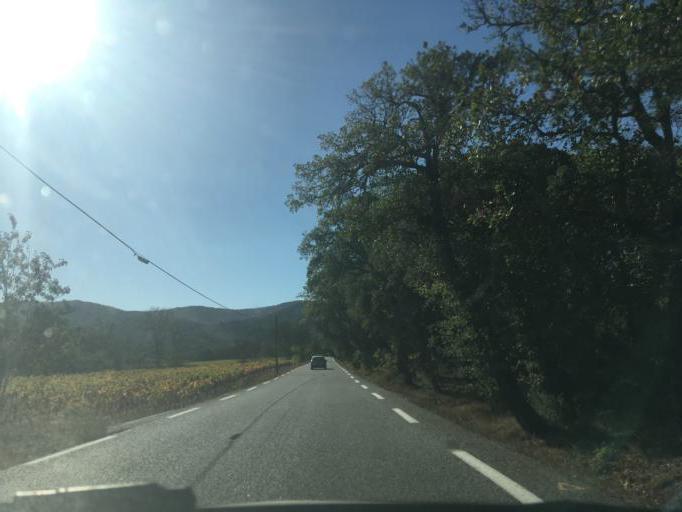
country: FR
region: Provence-Alpes-Cote d'Azur
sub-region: Departement du Var
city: La Garde-Freinet
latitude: 43.3468
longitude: 6.4279
